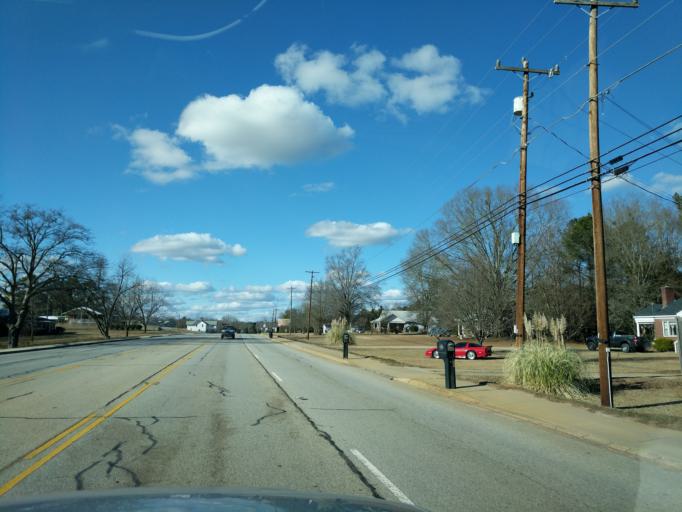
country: US
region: South Carolina
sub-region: Greenwood County
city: Greenwood
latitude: 34.1275
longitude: -82.1227
